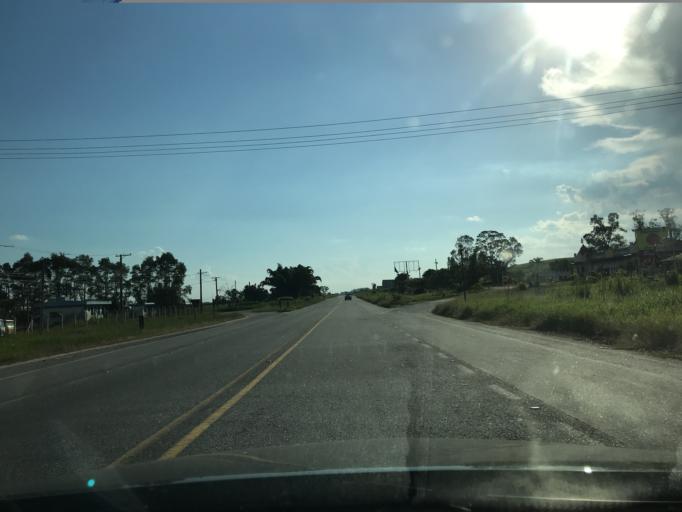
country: BR
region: Sao Paulo
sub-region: Tremembe
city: Tremembe
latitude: -22.9443
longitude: -45.6052
